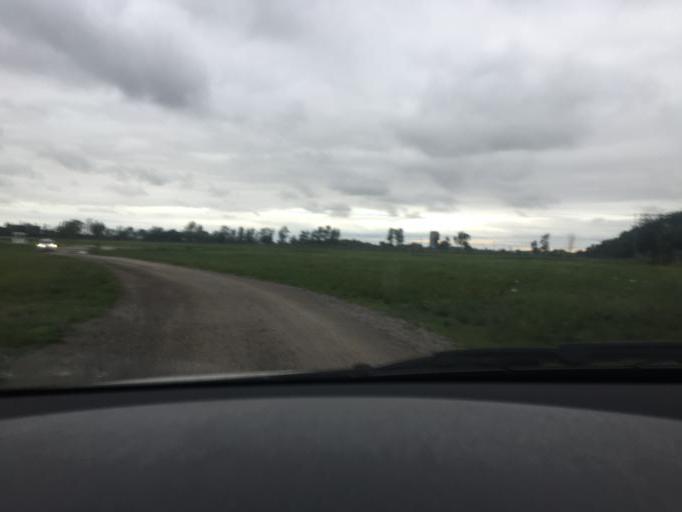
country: AR
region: Cordoba
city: Villa Allende
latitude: -31.3122
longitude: -64.2256
